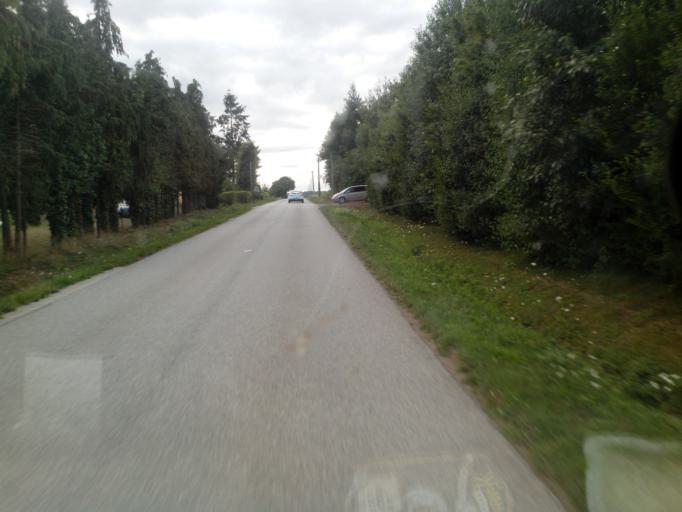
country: FR
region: Brittany
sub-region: Departement du Morbihan
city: Mauron
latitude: 48.0764
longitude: -2.2563
